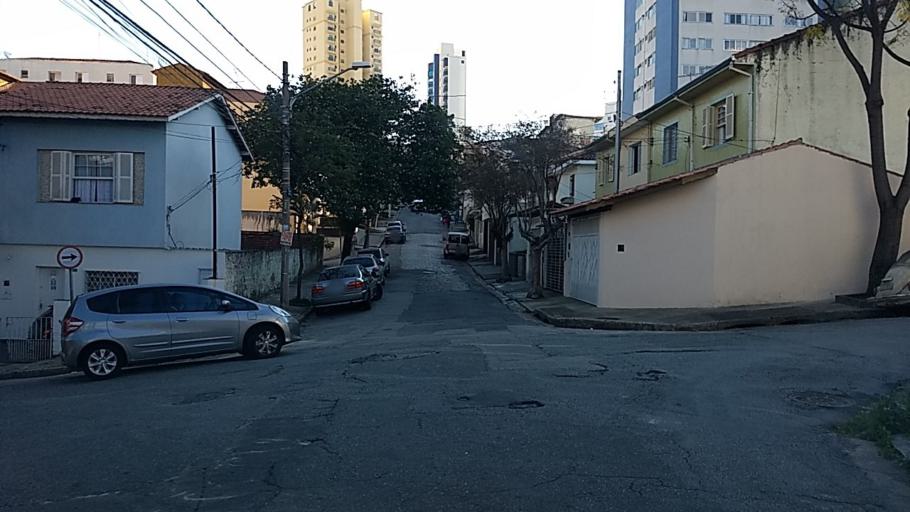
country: BR
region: Sao Paulo
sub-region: Sao Paulo
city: Sao Paulo
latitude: -23.4875
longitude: -46.6161
